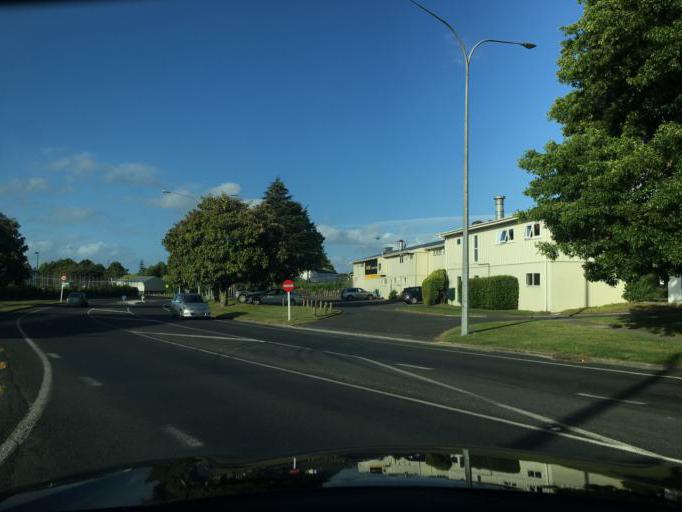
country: NZ
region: Waikato
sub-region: Waipa District
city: Cambridge
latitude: -38.0106
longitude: 175.3285
